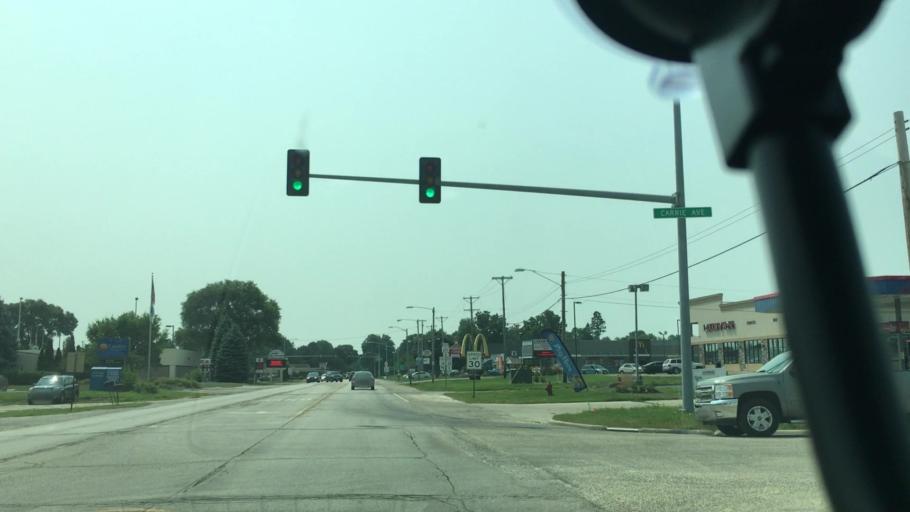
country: US
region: Illinois
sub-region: Ogle County
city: Rochelle
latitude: 41.9363
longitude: -89.0682
